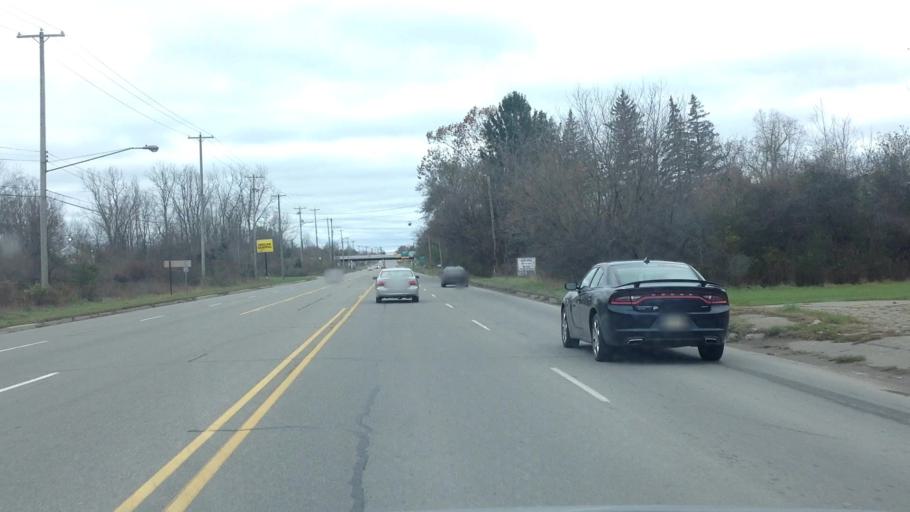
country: US
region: Michigan
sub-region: Genesee County
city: Mount Morris
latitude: 43.1044
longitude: -83.6944
